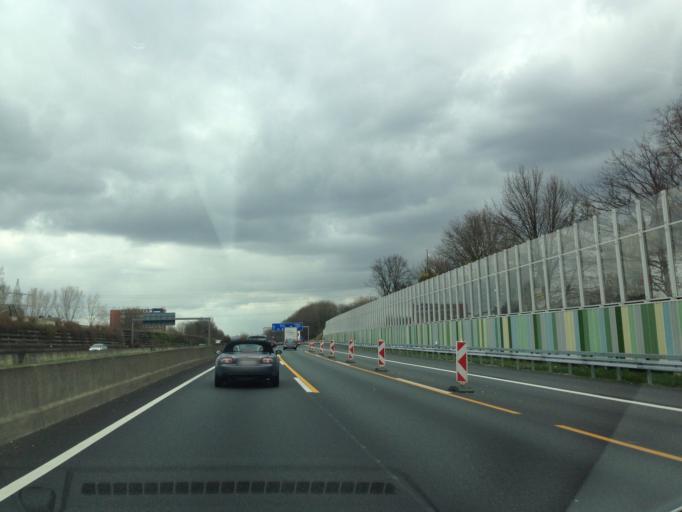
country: DE
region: North Rhine-Westphalia
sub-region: Regierungsbezirk Dusseldorf
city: Essen
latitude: 51.4595
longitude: 7.0524
